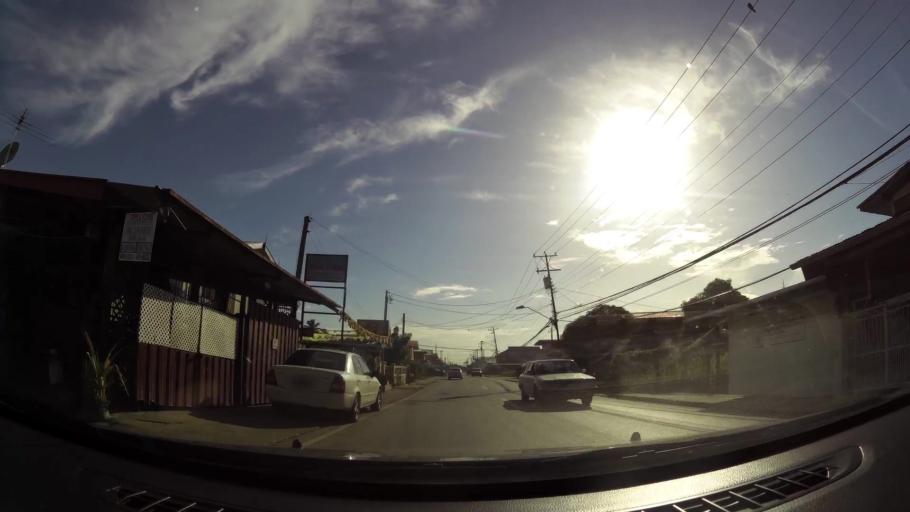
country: TT
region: Chaguanas
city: Chaguanas
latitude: 10.5662
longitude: -61.3780
